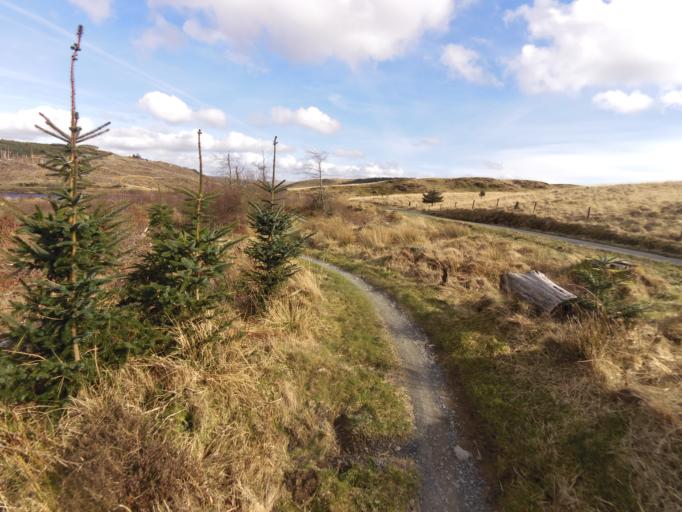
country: GB
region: Wales
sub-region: County of Ceredigion
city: Bow Street
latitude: 52.4342
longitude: -3.8948
